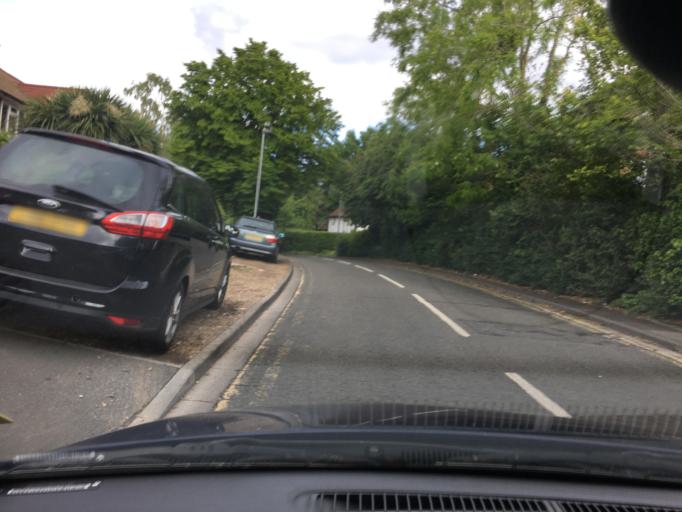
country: GB
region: England
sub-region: Bracknell Forest
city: Bracknell
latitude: 51.4004
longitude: -0.7572
